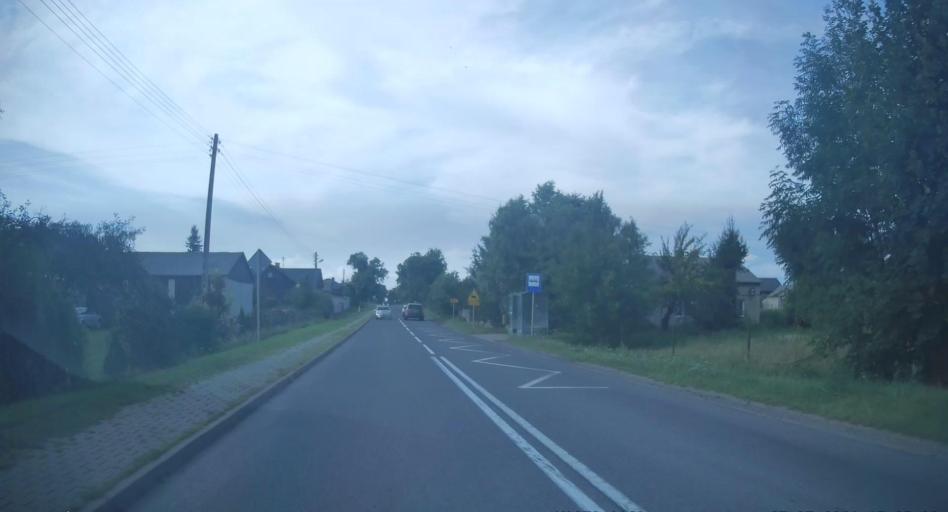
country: PL
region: Lodz Voivodeship
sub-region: Powiat tomaszowski
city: Rzeczyca
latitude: 51.6293
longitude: 20.2919
